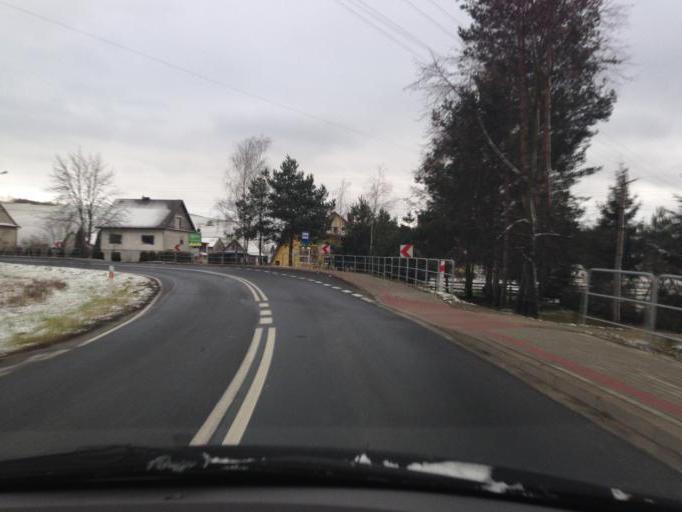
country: PL
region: Lesser Poland Voivodeship
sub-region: Powiat tarnowski
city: Gromnik
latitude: 49.8379
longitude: 20.9840
